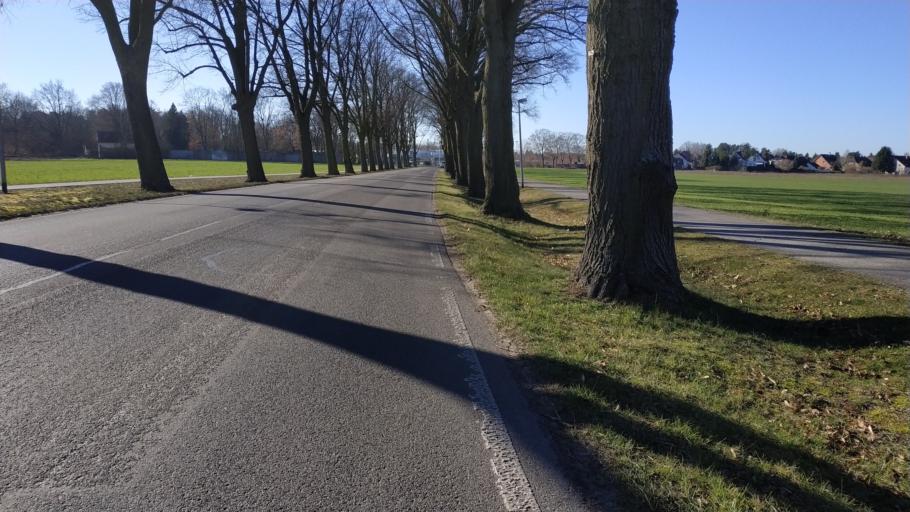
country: DE
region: Brandenburg
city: Petershagen
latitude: 52.5348
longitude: 13.8127
